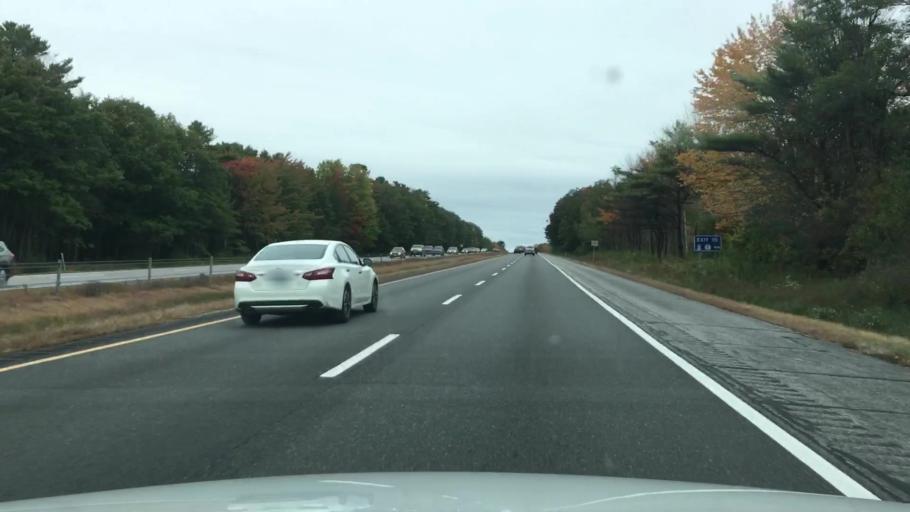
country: US
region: Maine
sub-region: Cumberland County
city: Yarmouth
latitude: 43.7761
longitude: -70.1984
